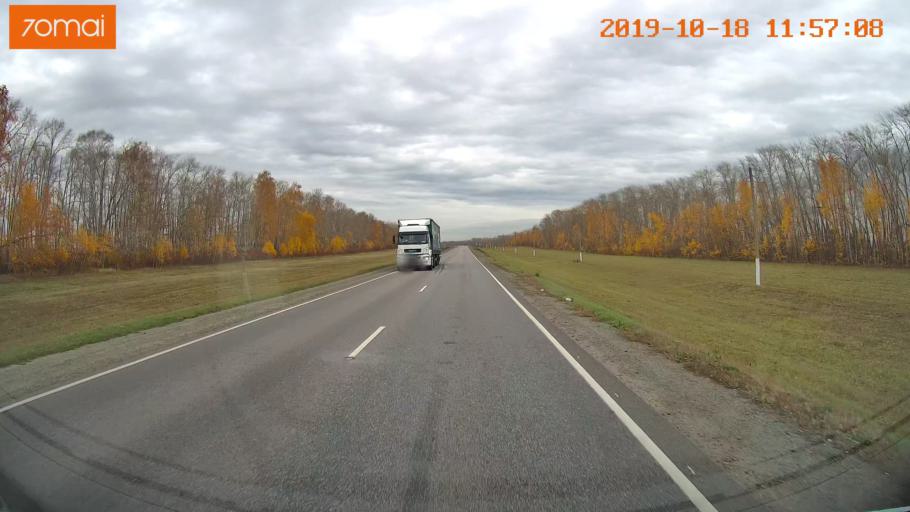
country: RU
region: Rjazan
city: Mikhaylov
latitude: 54.2661
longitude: 39.1350
